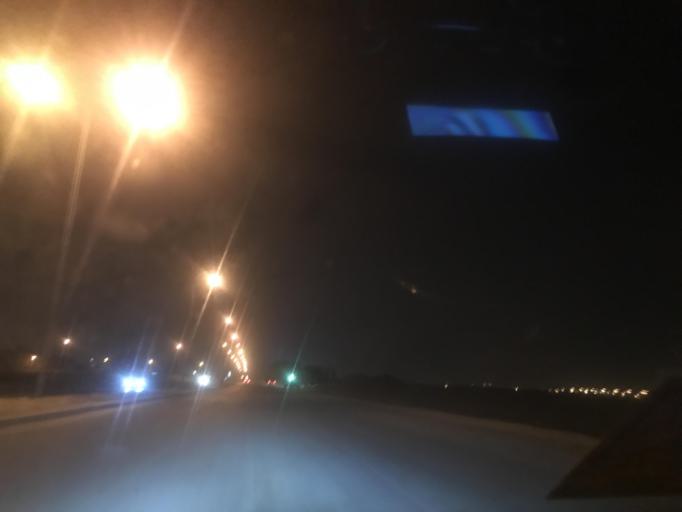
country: SA
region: Ar Riyad
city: Riyadh
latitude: 24.8126
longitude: 46.5873
